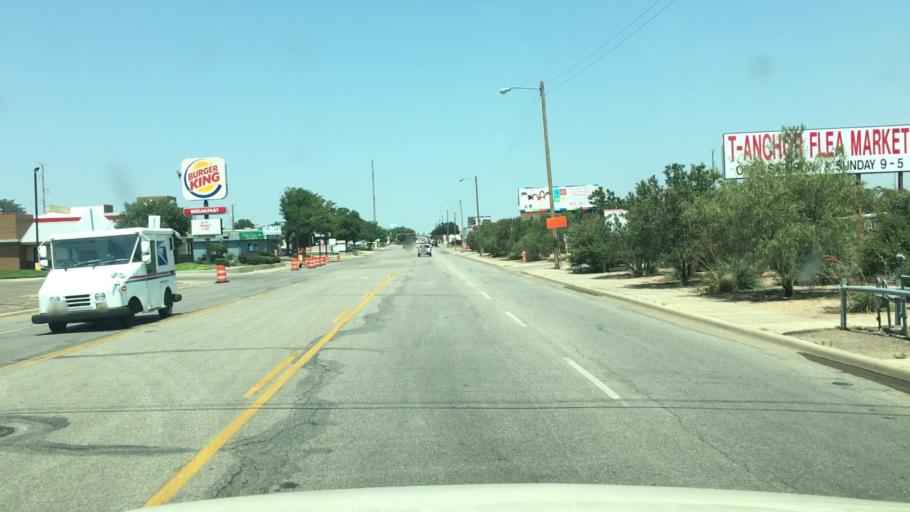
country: US
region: Texas
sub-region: Potter County
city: Amarillo
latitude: 35.1960
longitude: -101.8169
